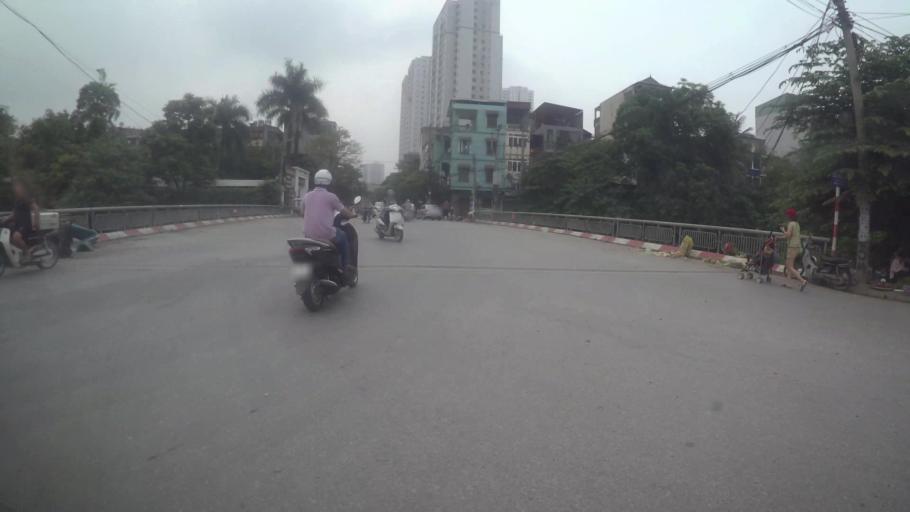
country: VN
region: Ha Noi
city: Ha Dong
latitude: 20.9709
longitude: 105.7674
